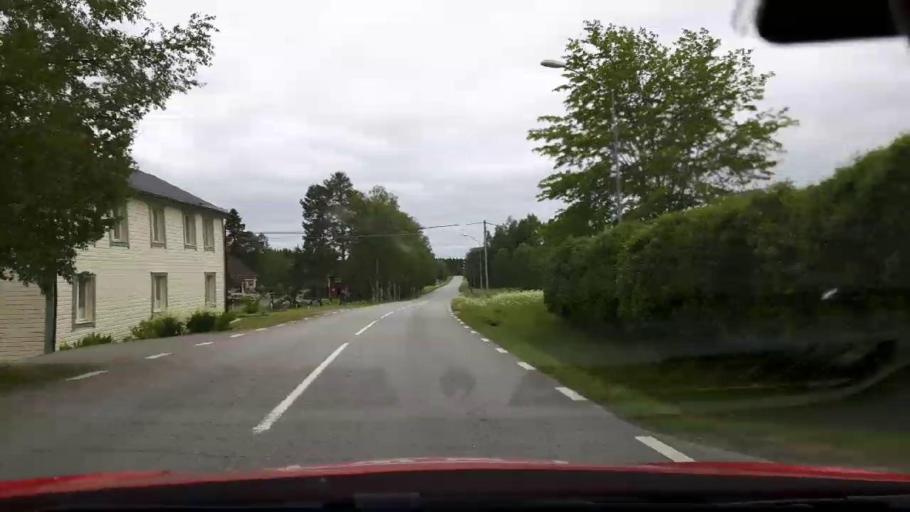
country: SE
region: Jaemtland
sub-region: Stroemsunds Kommun
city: Stroemsund
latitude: 63.5544
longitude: 15.4037
